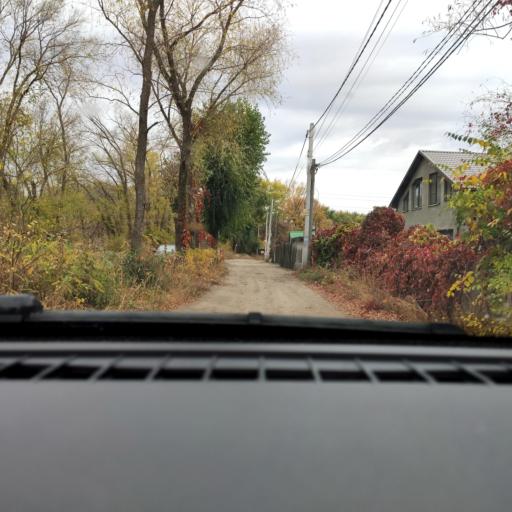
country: RU
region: Voronezj
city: Maslovka
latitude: 51.6018
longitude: 39.2313
